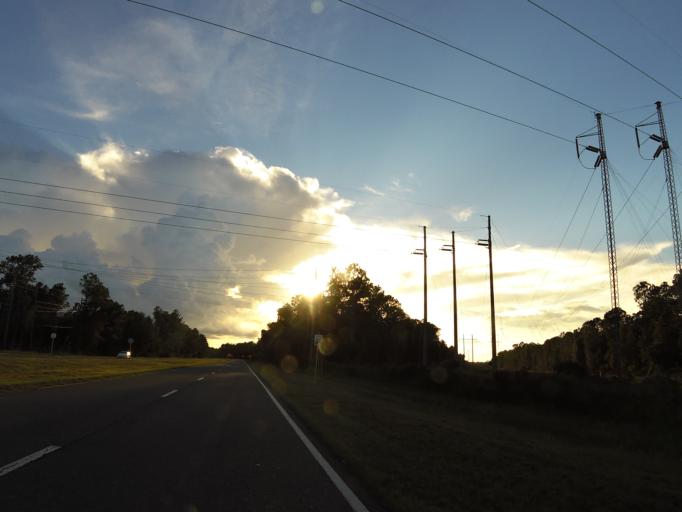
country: US
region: Georgia
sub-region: Camden County
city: Kings Bay Base
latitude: 30.7911
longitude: -81.5867
